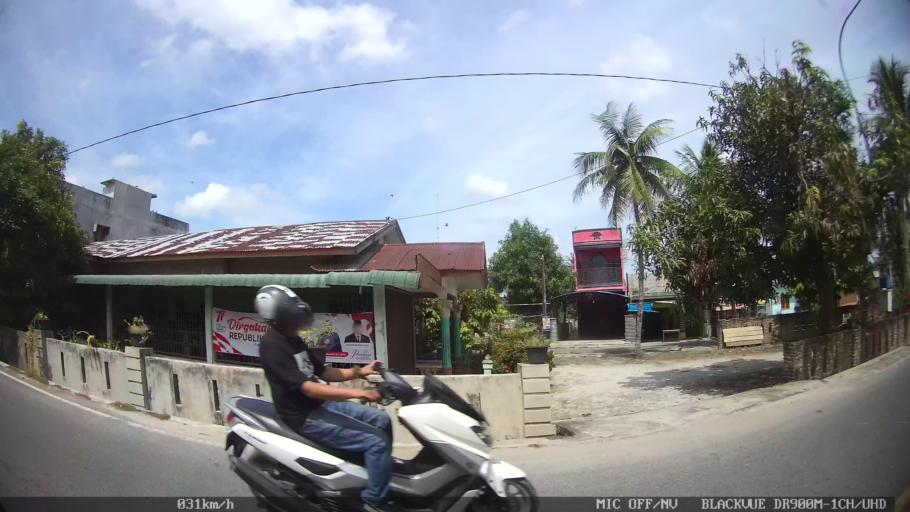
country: ID
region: North Sumatra
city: Percut
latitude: 3.5974
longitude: 98.8601
